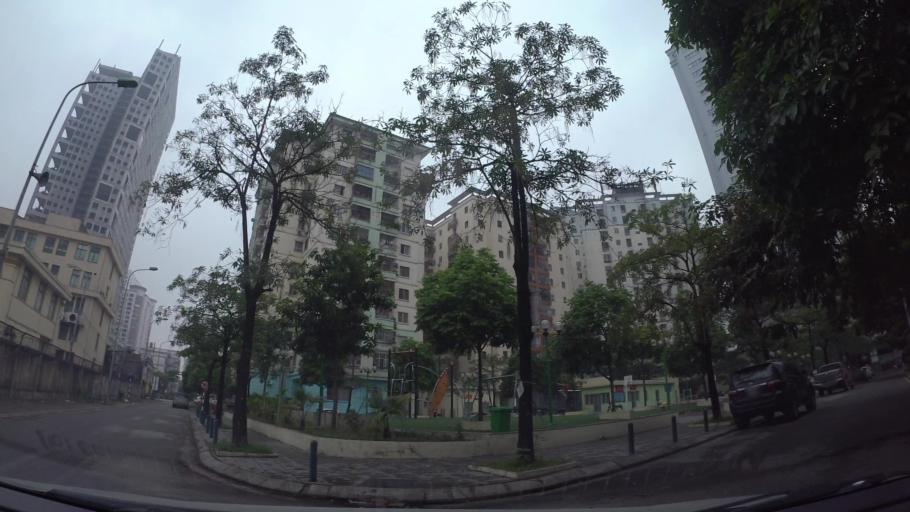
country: VN
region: Ha Noi
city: Cau Giay
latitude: 21.0229
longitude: 105.7877
